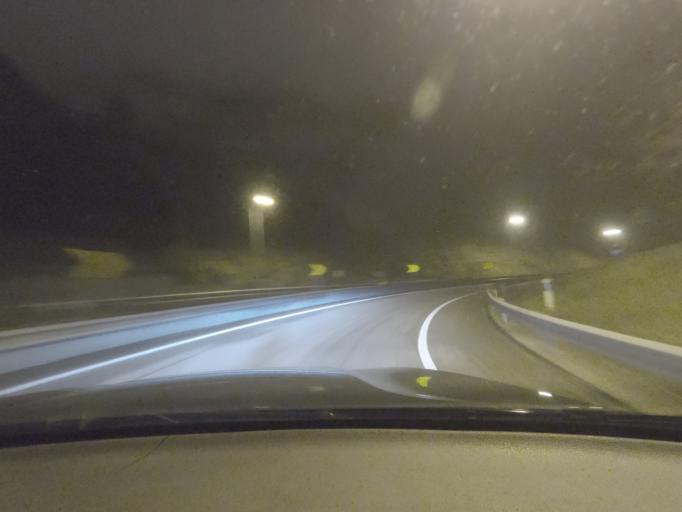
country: PT
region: Vila Real
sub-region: Vila Real
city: Vila Real
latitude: 41.3046
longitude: -7.7504
